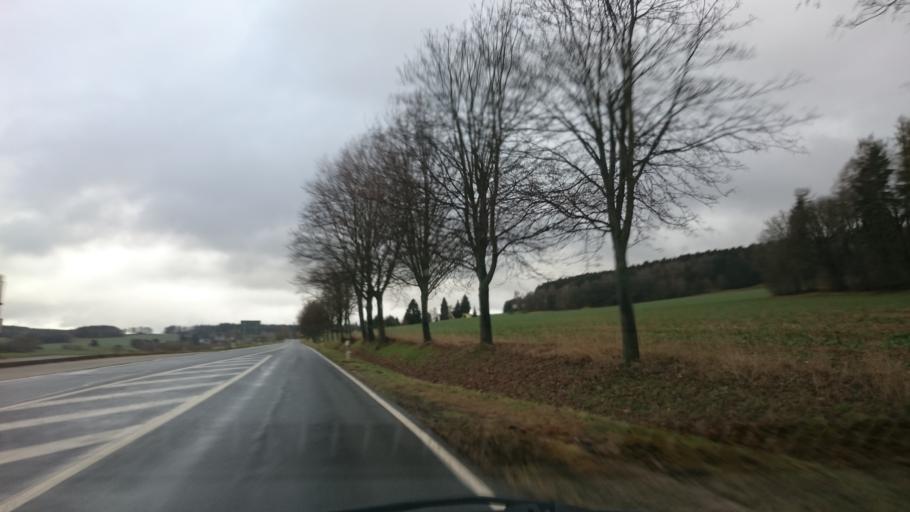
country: DE
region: Saxony
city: Kirchberg
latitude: 50.6261
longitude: 12.5722
